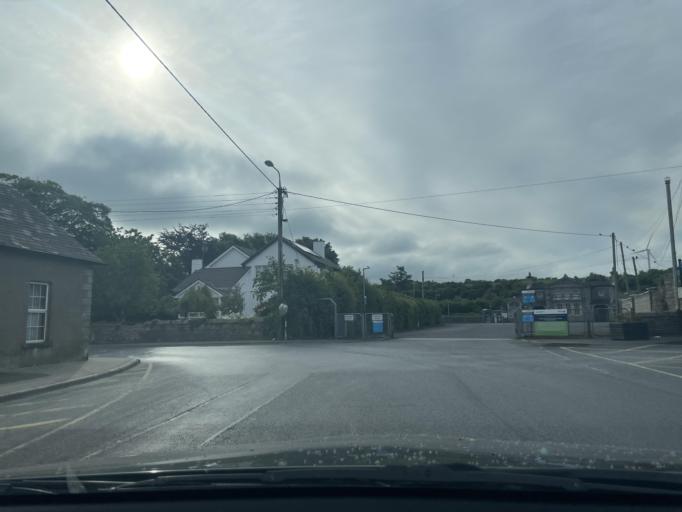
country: IE
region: Leinster
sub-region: County Carlow
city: Bagenalstown
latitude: 52.6998
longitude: -6.9537
